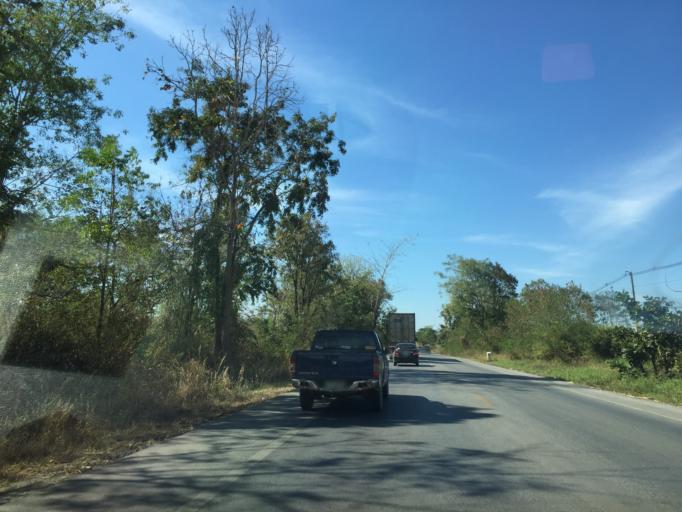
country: TH
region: Changwat Nong Bua Lamphu
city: Na Klang
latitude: 17.3138
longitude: 102.1668
